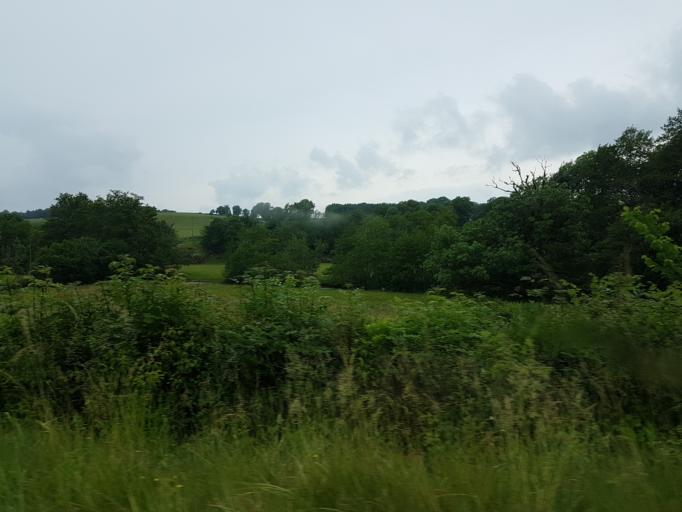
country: FR
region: Bourgogne
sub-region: Departement de la Nievre
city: Corbigny
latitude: 47.1905
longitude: 3.7354
